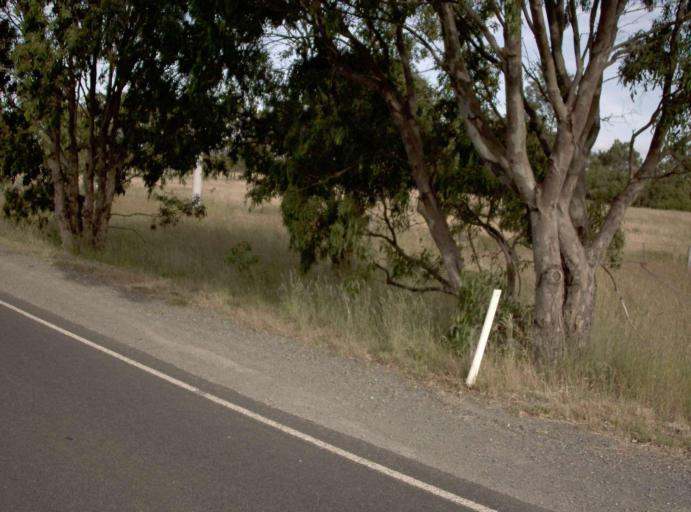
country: AU
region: Victoria
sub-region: Wellington
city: Heyfield
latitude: -38.0586
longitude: 146.6609
